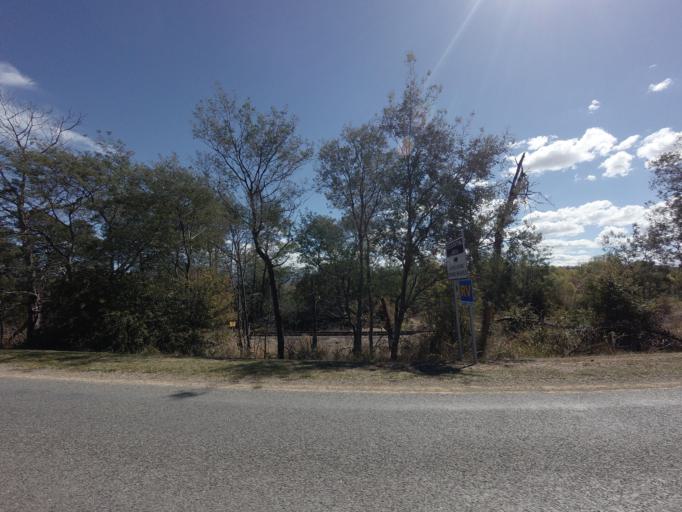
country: AU
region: Tasmania
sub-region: Break O'Day
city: St Helens
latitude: -41.6434
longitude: 147.9620
